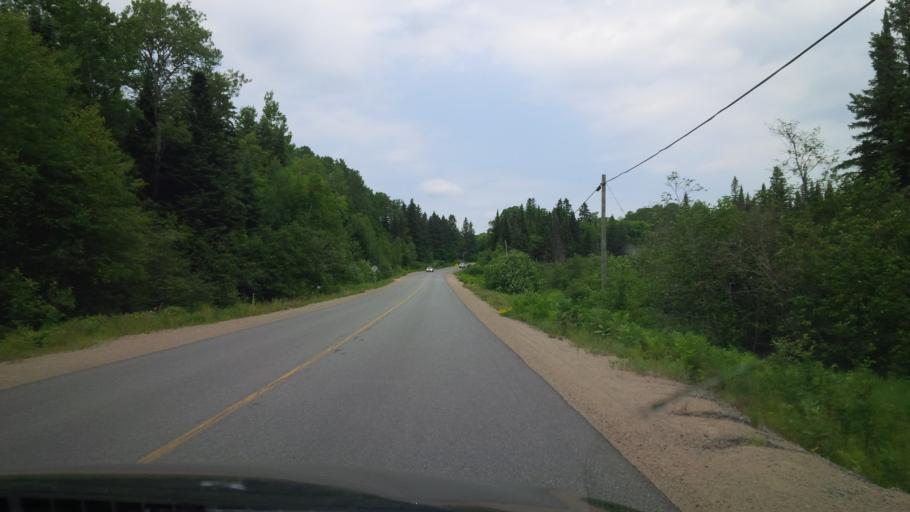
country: CA
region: Ontario
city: Huntsville
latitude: 45.6046
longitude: -79.1767
